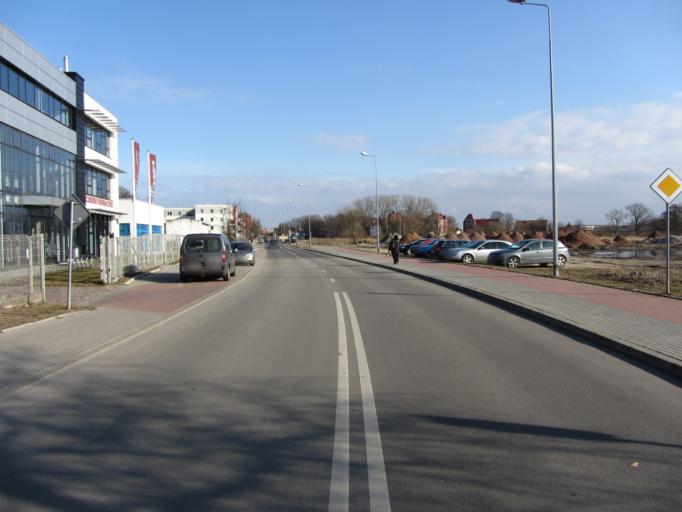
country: PL
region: West Pomeranian Voivodeship
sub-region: Powiat kolobrzeski
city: Kolobrzeg
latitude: 54.1712
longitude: 15.5567
